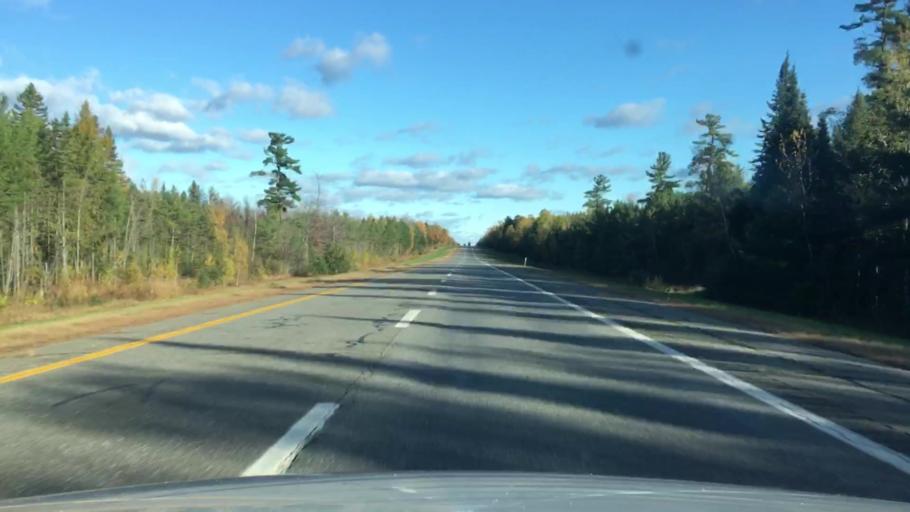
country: US
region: Maine
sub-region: Penobscot County
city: Greenbush
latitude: 45.0624
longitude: -68.6887
